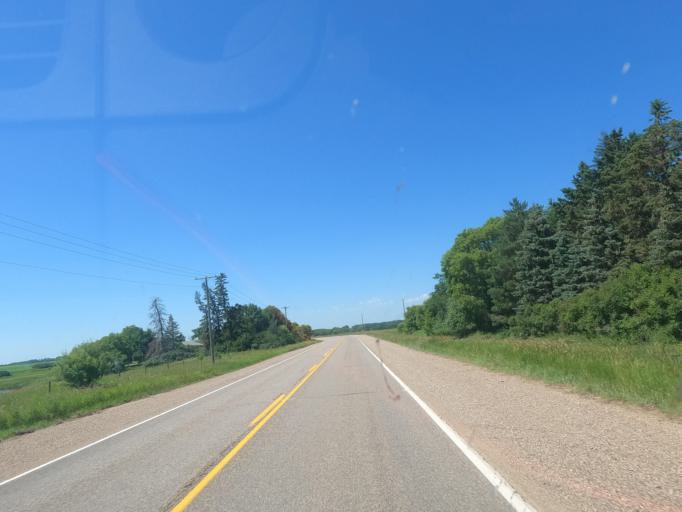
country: CA
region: Manitoba
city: Souris
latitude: 49.6211
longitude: -100.2817
